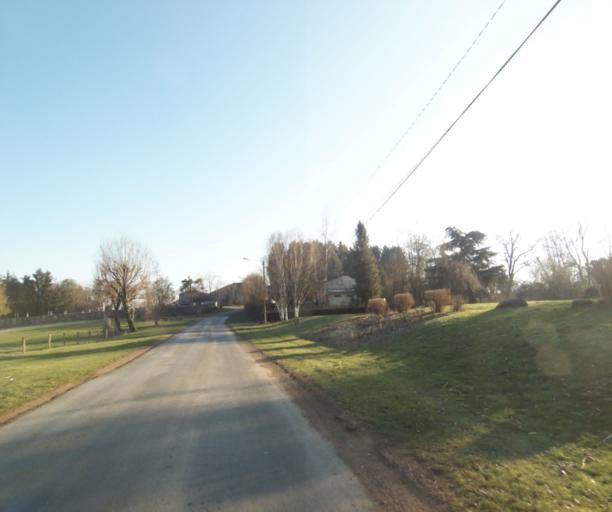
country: FR
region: Champagne-Ardenne
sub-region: Departement de la Haute-Marne
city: Bienville
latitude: 48.5873
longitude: 5.0851
